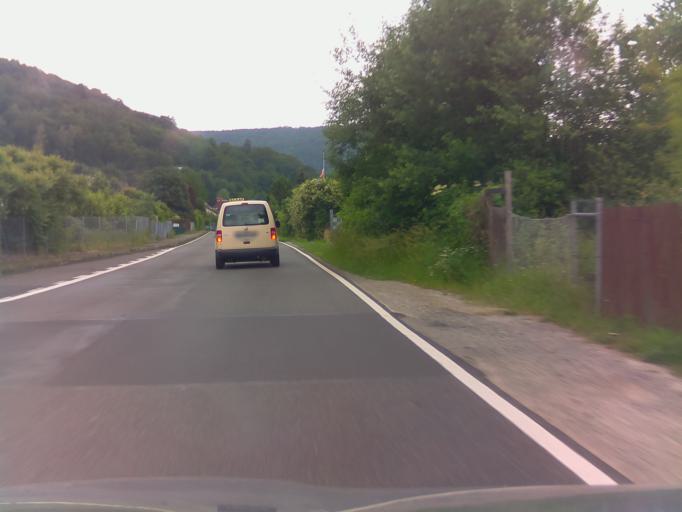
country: DE
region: Bavaria
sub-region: Regierungsbezirk Unterfranken
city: Gemunden
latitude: 50.0651
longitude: 9.7032
